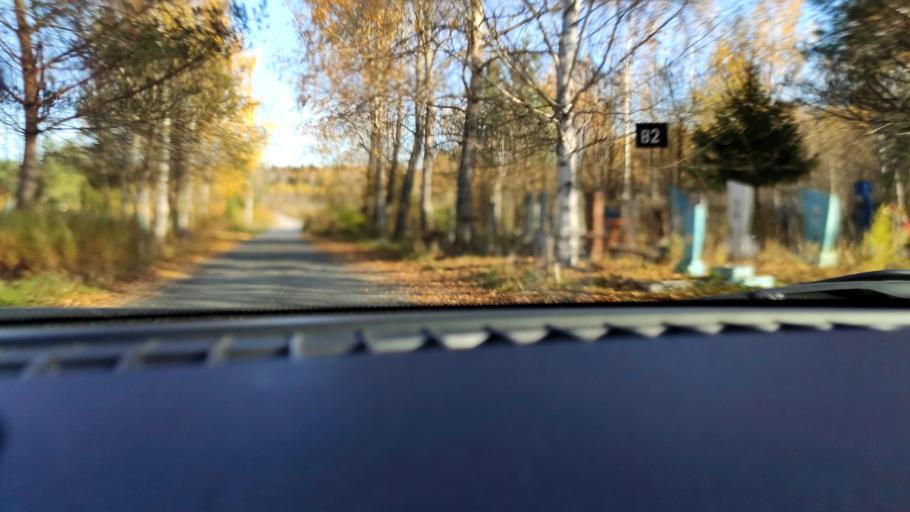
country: RU
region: Perm
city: Kondratovo
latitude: 58.0671
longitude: 56.1373
